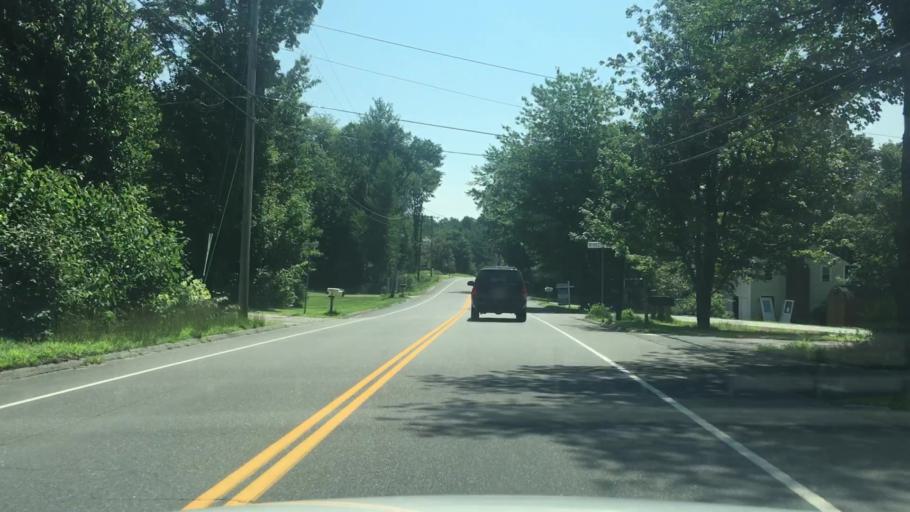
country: US
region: Maine
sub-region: Cumberland County
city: Cumberland Center
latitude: 43.8027
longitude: -70.2708
